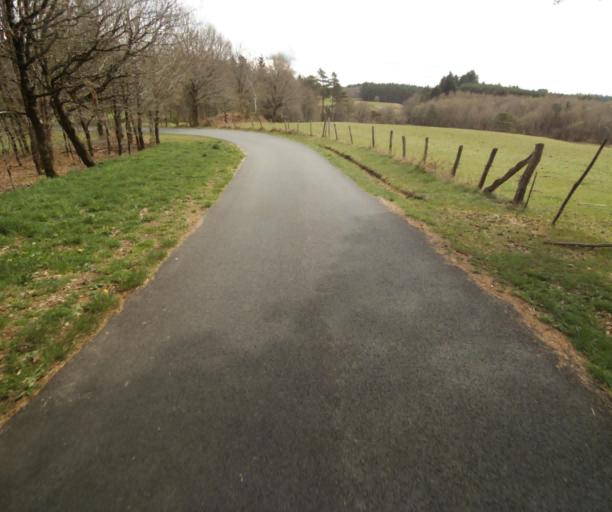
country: FR
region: Limousin
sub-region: Departement de la Correze
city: Correze
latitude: 45.3410
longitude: 1.9567
